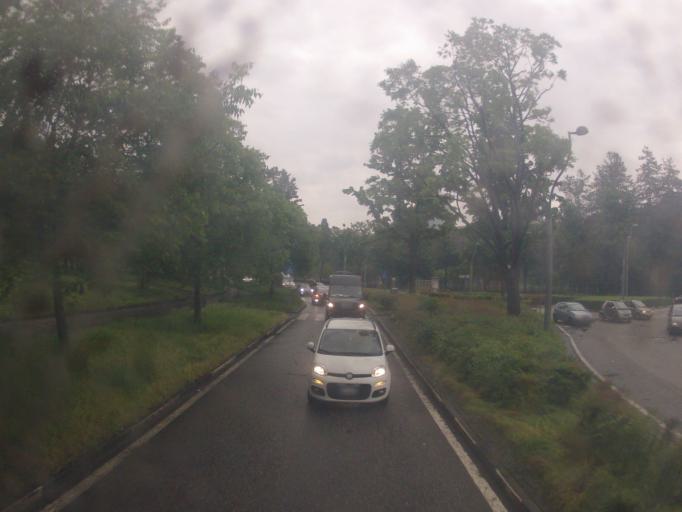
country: IT
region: Piedmont
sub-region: Provincia di Torino
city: Moncalieri
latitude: 45.0171
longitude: 7.6679
